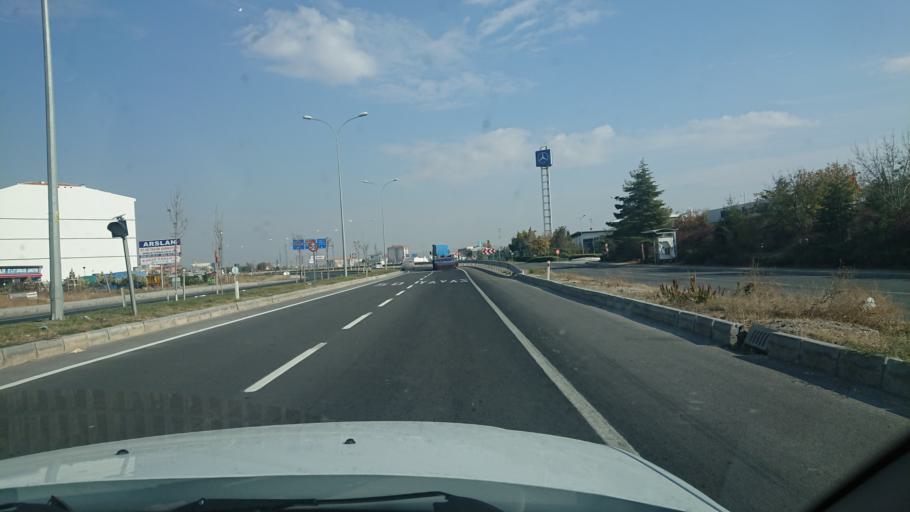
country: TR
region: Aksaray
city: Aksaray
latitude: 38.3530
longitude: 33.9668
